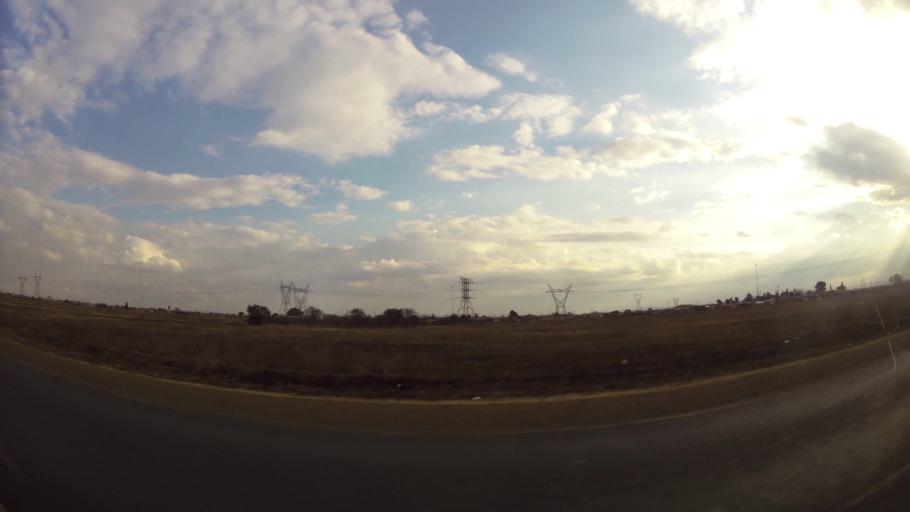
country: ZA
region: Gauteng
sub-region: Sedibeng District Municipality
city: Vanderbijlpark
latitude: -26.6748
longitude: 27.7919
